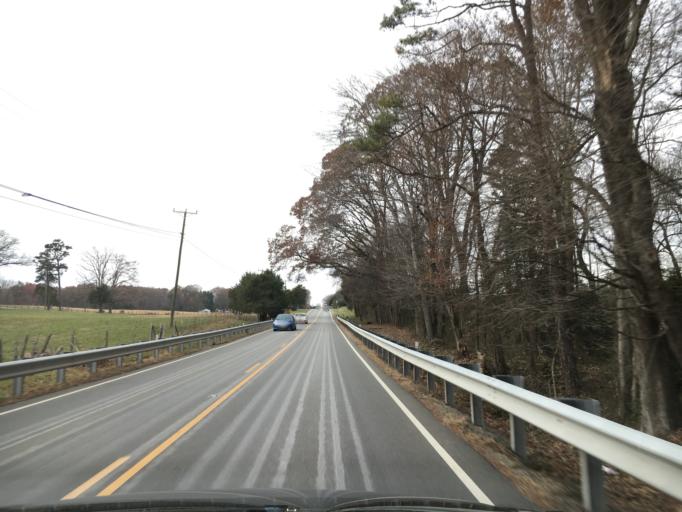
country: US
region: Virginia
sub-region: Henrico County
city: Wyndham
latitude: 37.6830
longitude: -77.7324
